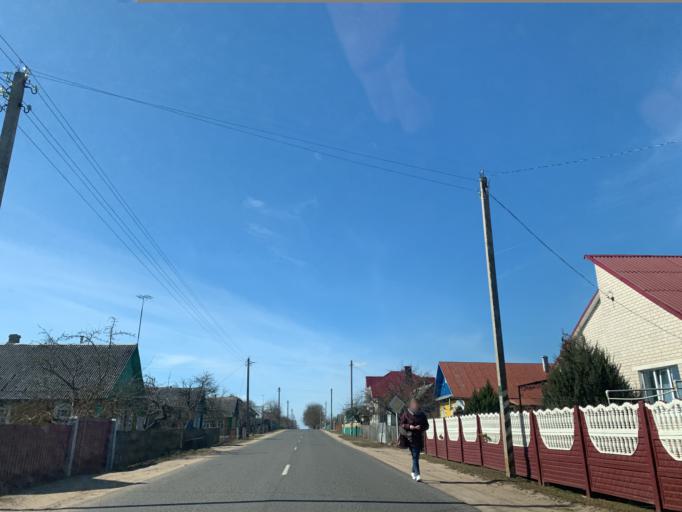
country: BY
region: Minsk
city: Haradzyeya
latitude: 53.3118
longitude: 26.5460
